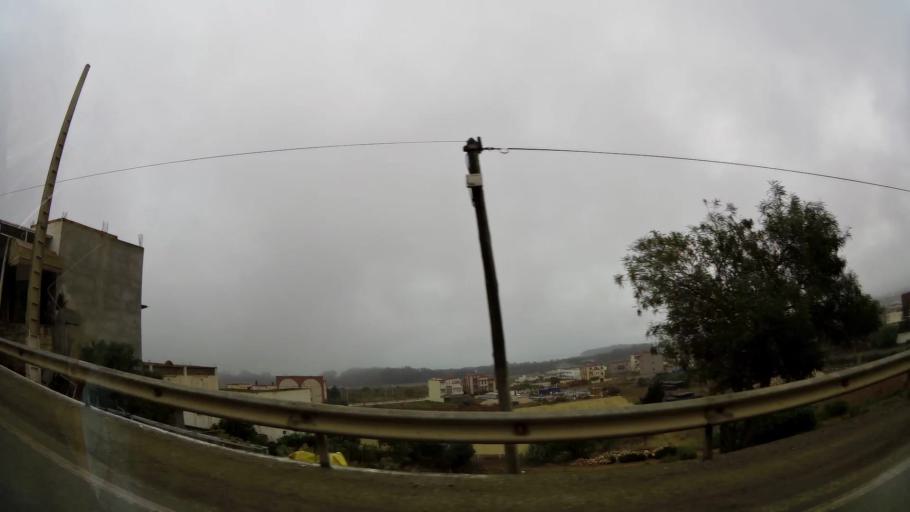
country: MA
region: Taza-Al Hoceima-Taounate
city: Imzourene
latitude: 35.1970
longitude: -3.8988
